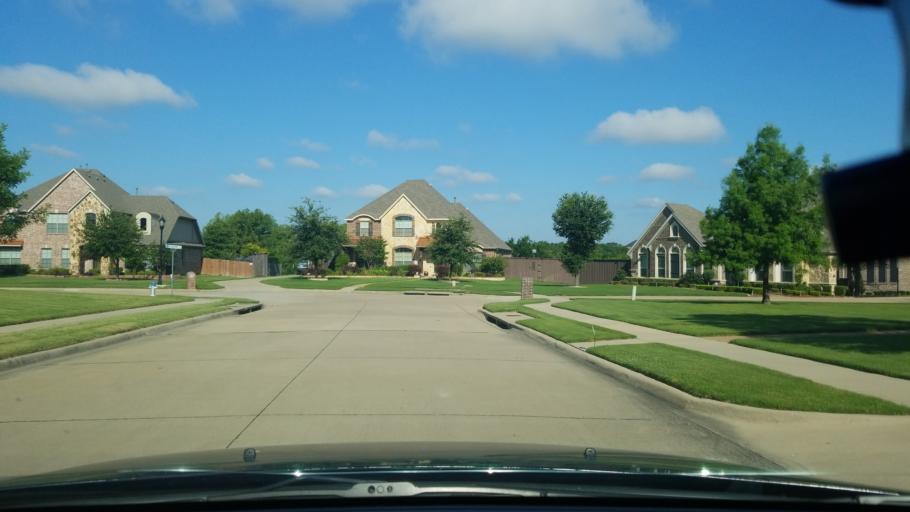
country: US
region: Texas
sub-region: Dallas County
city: Sunnyvale
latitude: 32.8092
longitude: -96.5627
